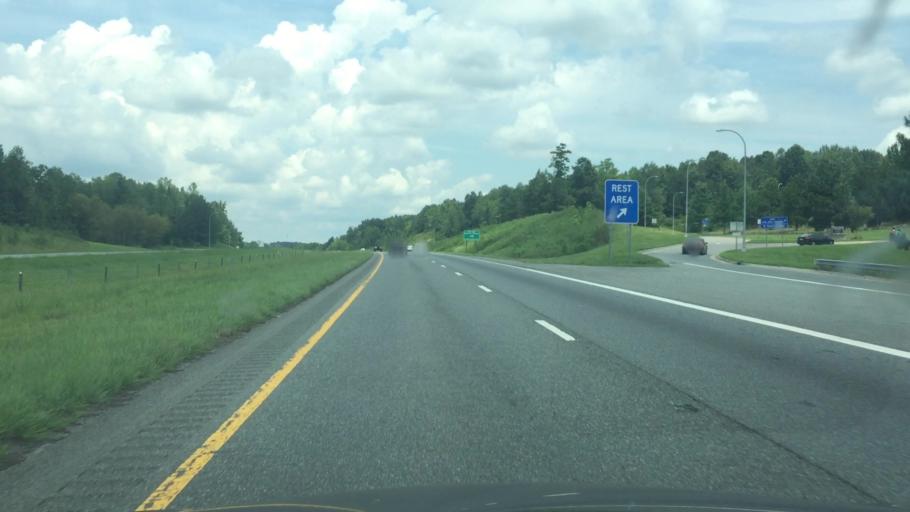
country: US
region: North Carolina
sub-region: Montgomery County
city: Biscoe
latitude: 35.5131
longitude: -79.7812
